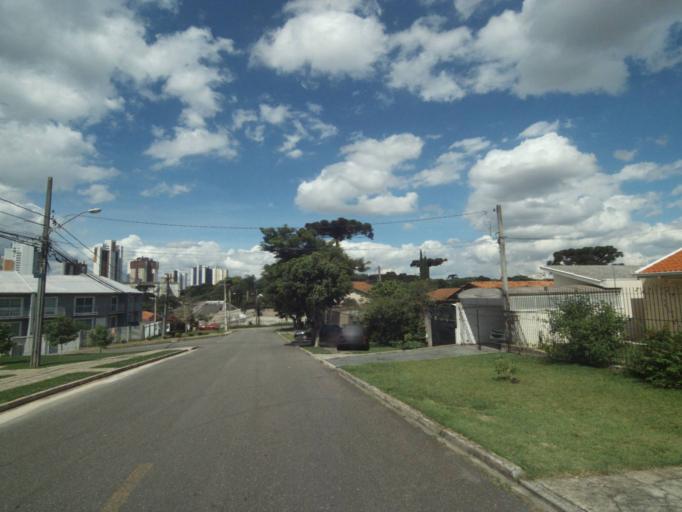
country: BR
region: Parana
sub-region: Curitiba
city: Curitiba
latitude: -25.4425
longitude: -49.3282
